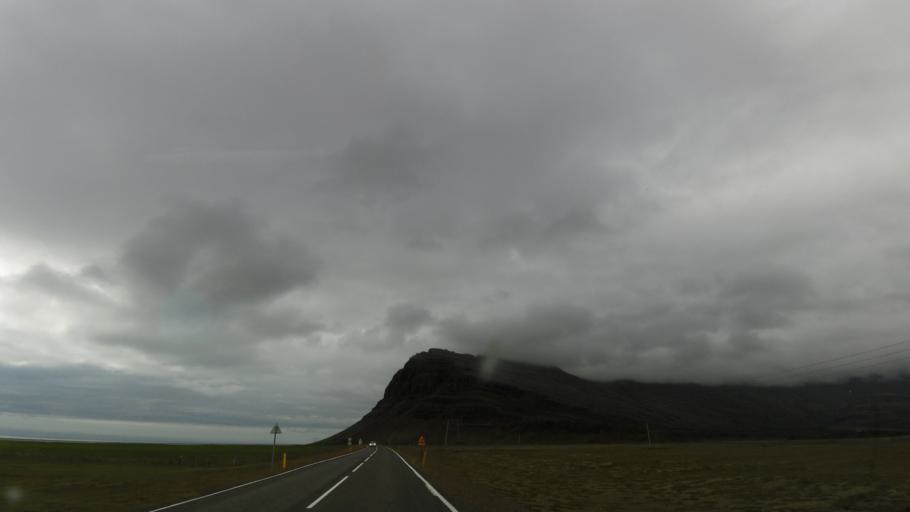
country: IS
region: East
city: Hoefn
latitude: 64.1568
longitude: -15.9417
